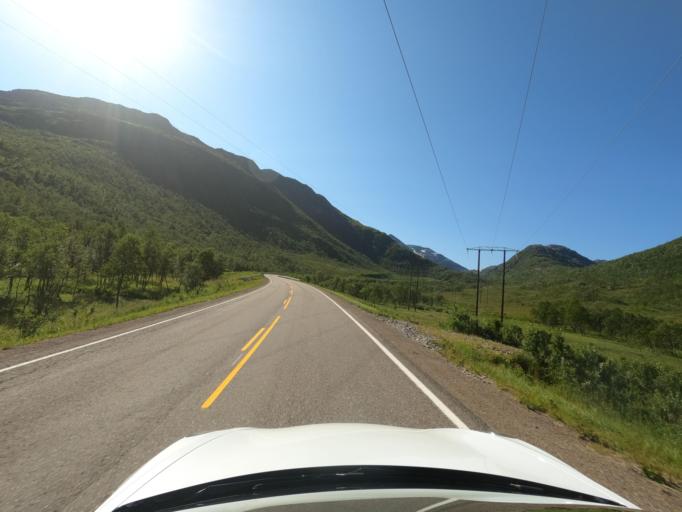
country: NO
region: Nordland
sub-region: Lodingen
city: Lodingen
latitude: 68.4958
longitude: 15.6995
